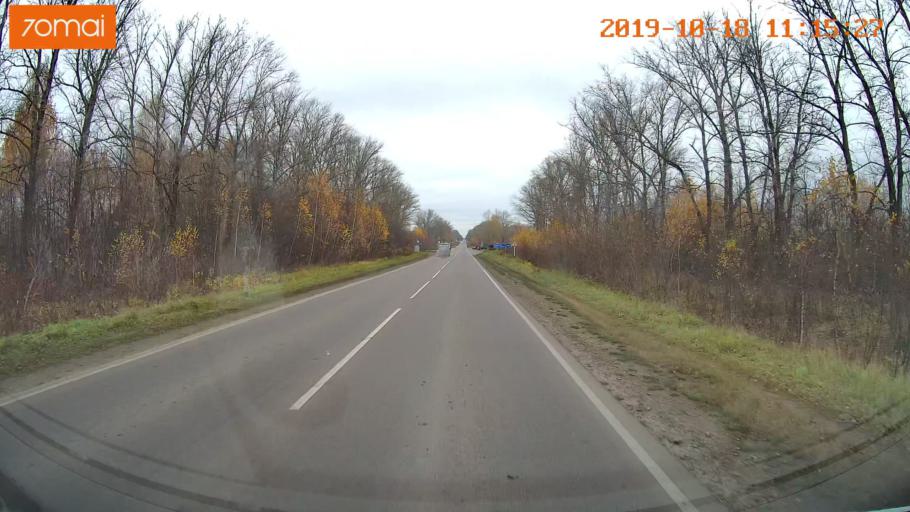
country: RU
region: Tula
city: Kimovsk
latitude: 53.9926
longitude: 38.5475
